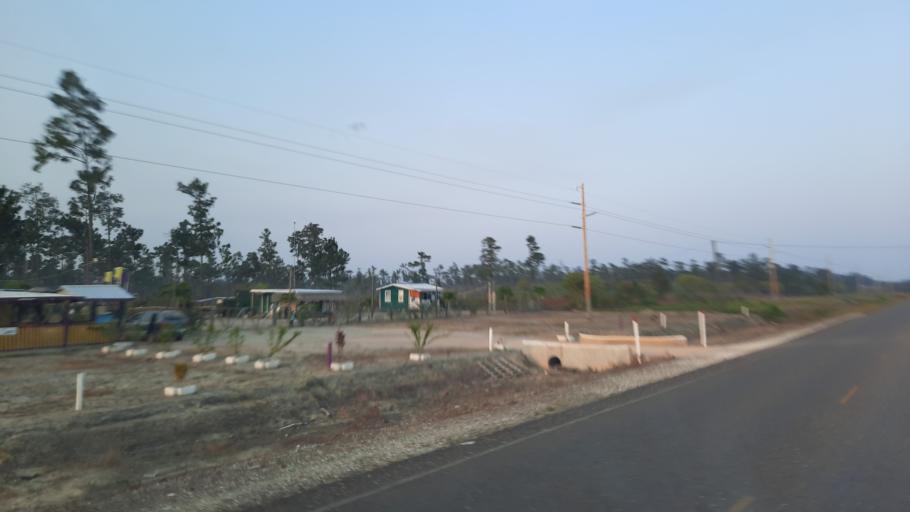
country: BZ
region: Stann Creek
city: Placencia
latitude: 16.5316
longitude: -88.4606
